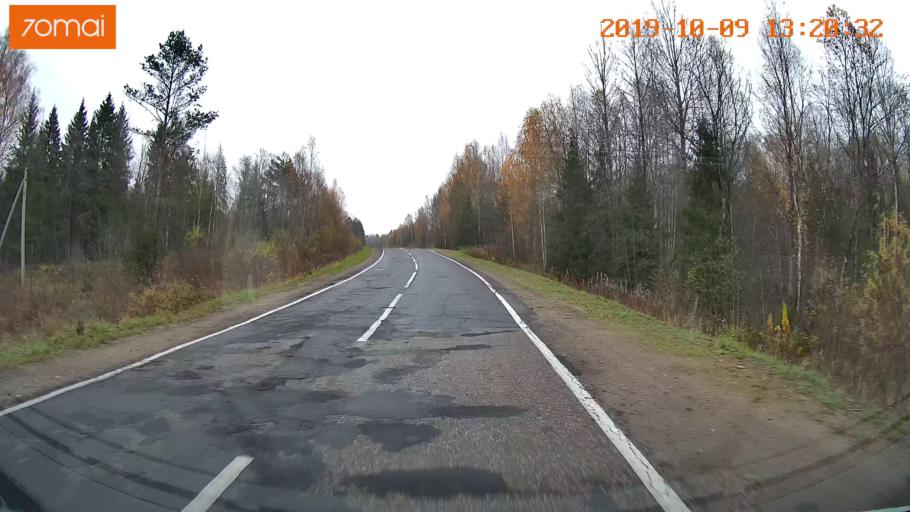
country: RU
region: Jaroslavl
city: Lyubim
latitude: 58.3425
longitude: 40.8306
